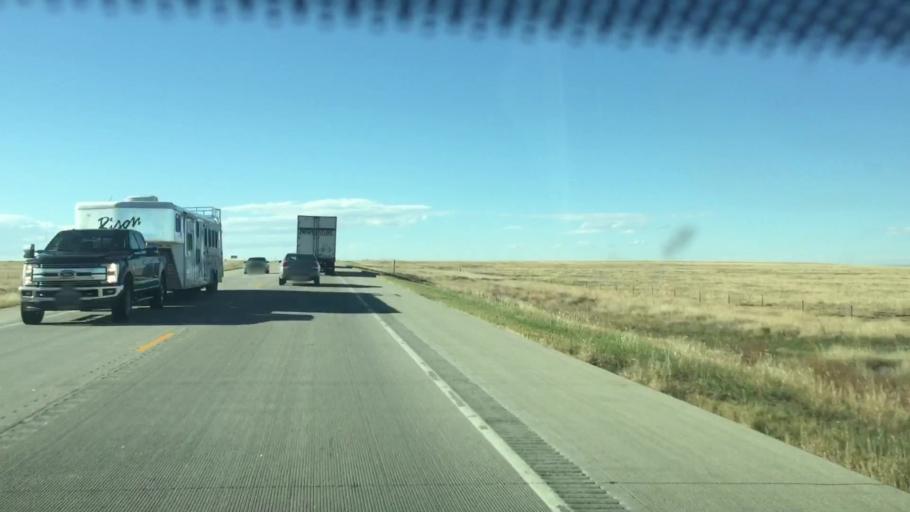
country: US
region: Colorado
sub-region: Lincoln County
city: Hugo
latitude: 38.9214
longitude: -103.1861
